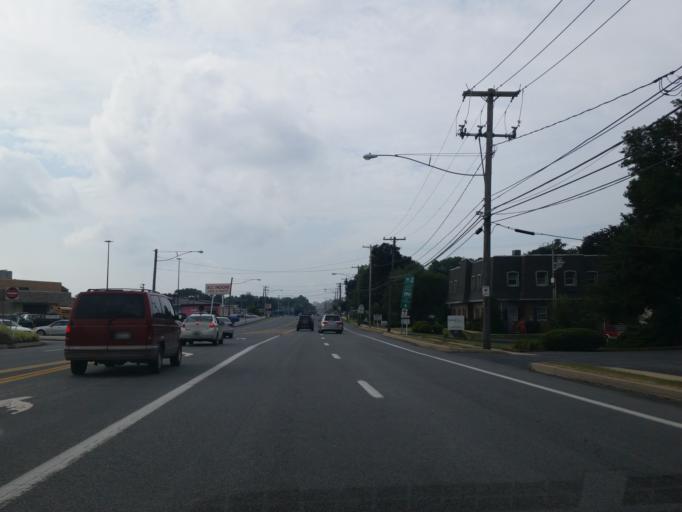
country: US
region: Pennsylvania
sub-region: Lancaster County
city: Lancaster
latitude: 40.0671
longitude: -76.3073
